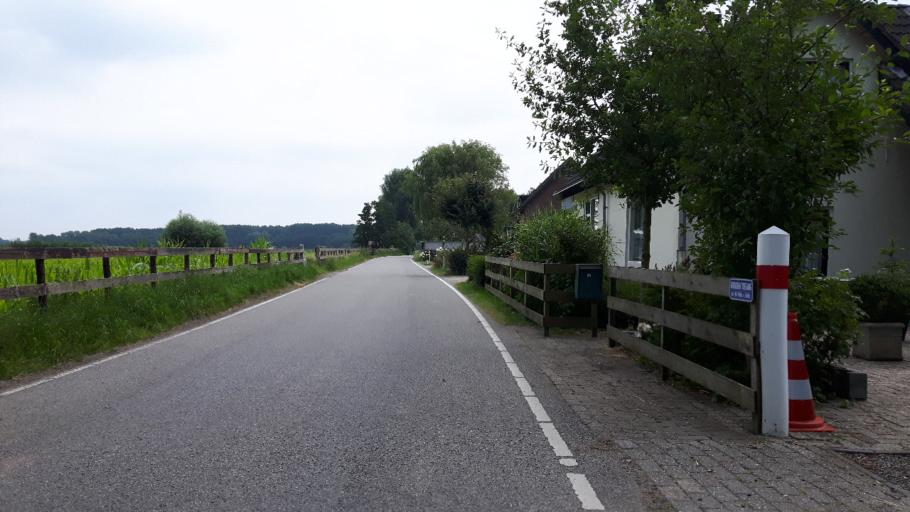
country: NL
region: Utrecht
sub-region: Gemeente IJsselstein
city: IJsselstein
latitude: 52.0451
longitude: 5.0240
